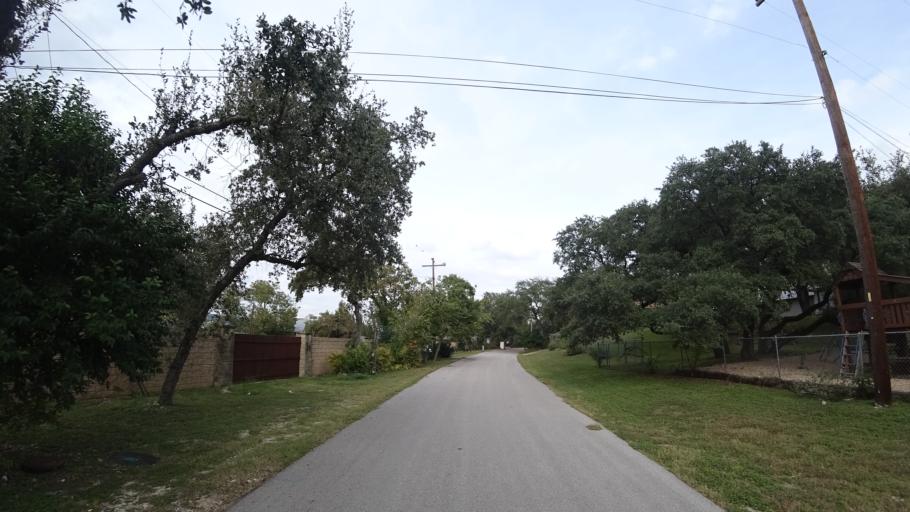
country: US
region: Texas
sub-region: Travis County
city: Hudson Bend
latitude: 30.3927
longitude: -97.8891
